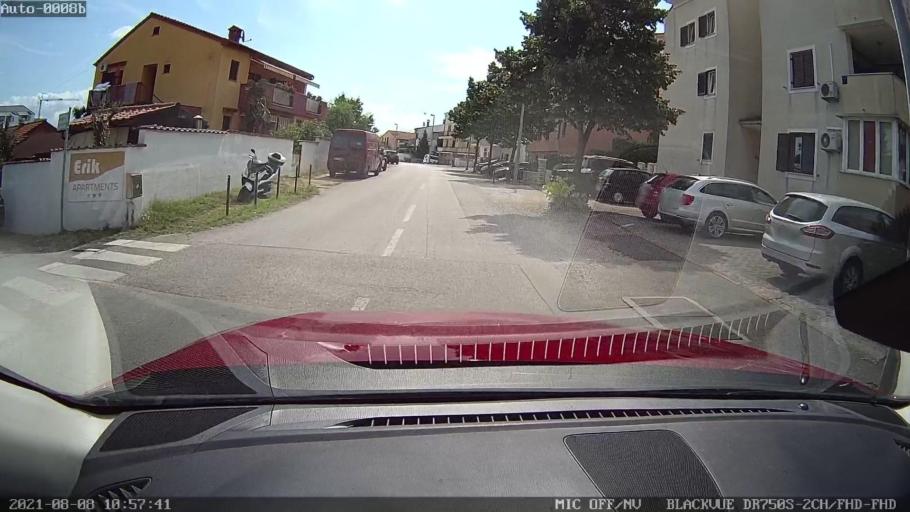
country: HR
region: Istarska
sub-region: Grad Rovinj
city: Rovinj
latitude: 45.0845
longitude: 13.6454
